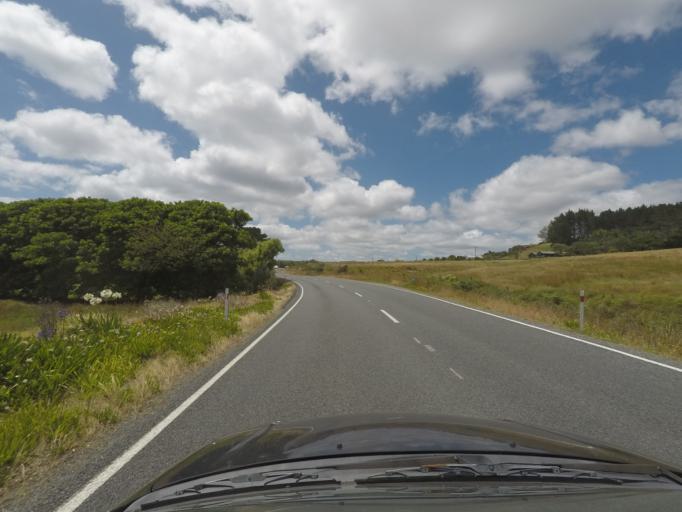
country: NZ
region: Northland
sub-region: Whangarei
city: Ruakaka
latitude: -36.0160
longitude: 174.4889
